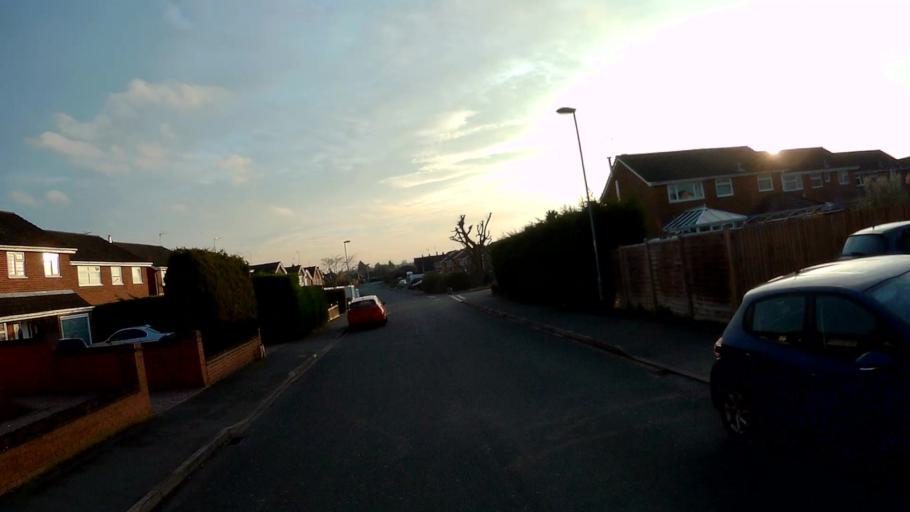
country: GB
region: England
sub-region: Lincolnshire
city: Bourne
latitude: 52.7770
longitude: -0.3801
